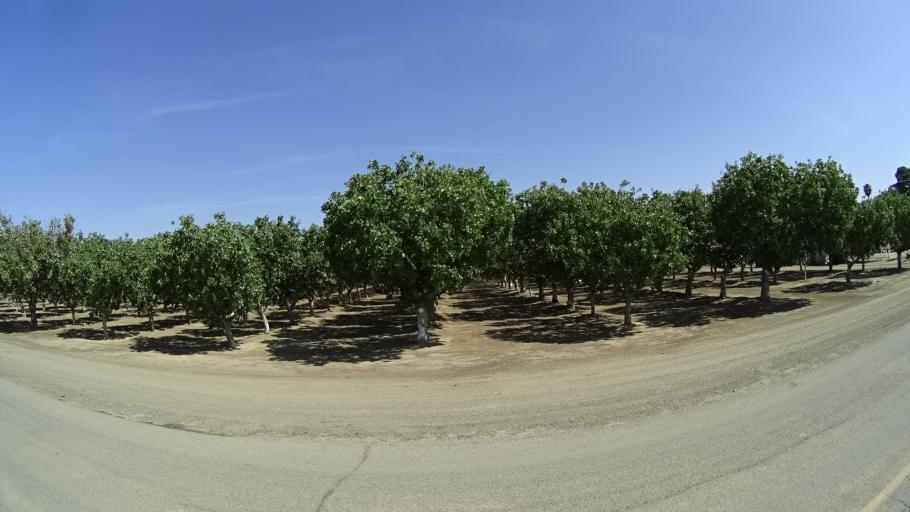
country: US
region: California
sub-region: Kings County
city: Kettleman City
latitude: 36.0725
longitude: -120.0331
